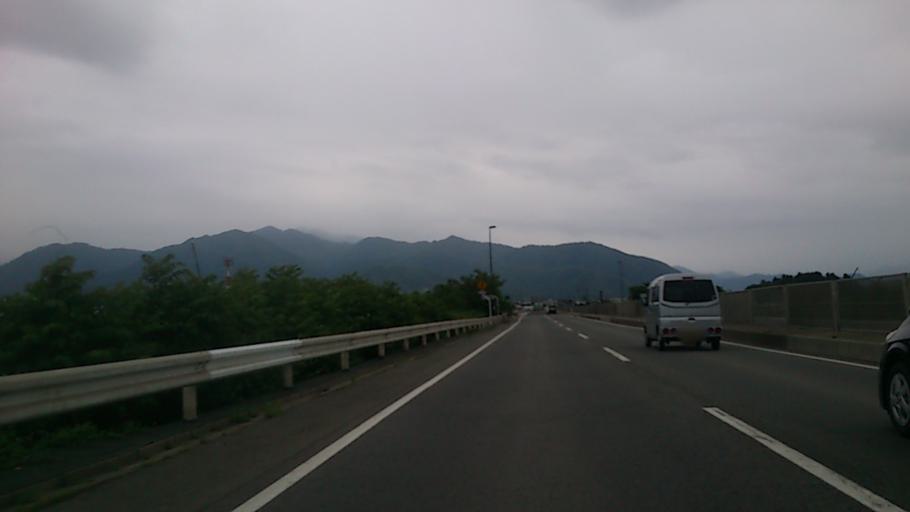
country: JP
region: Yamagata
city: Tendo
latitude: 38.3967
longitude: 140.3765
